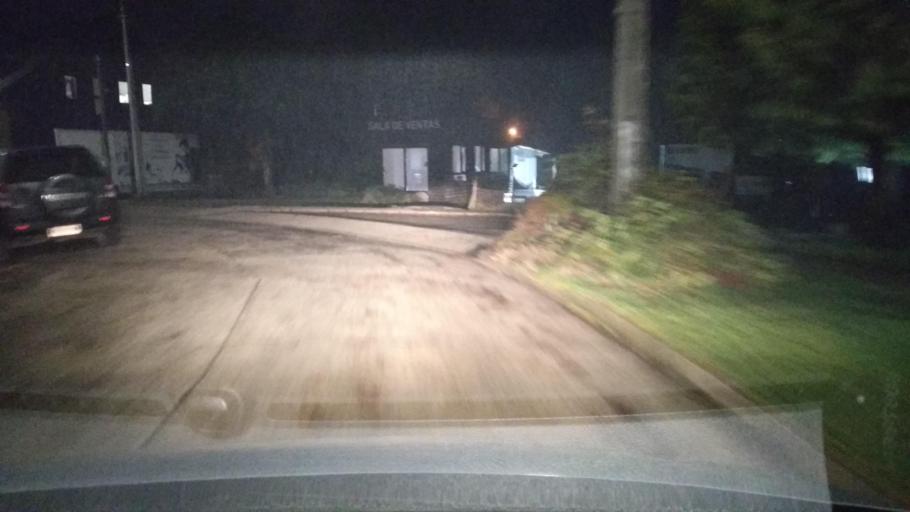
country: CL
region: Los Rios
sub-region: Provincia de Valdivia
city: Valdivia
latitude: -39.8163
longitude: -73.2585
